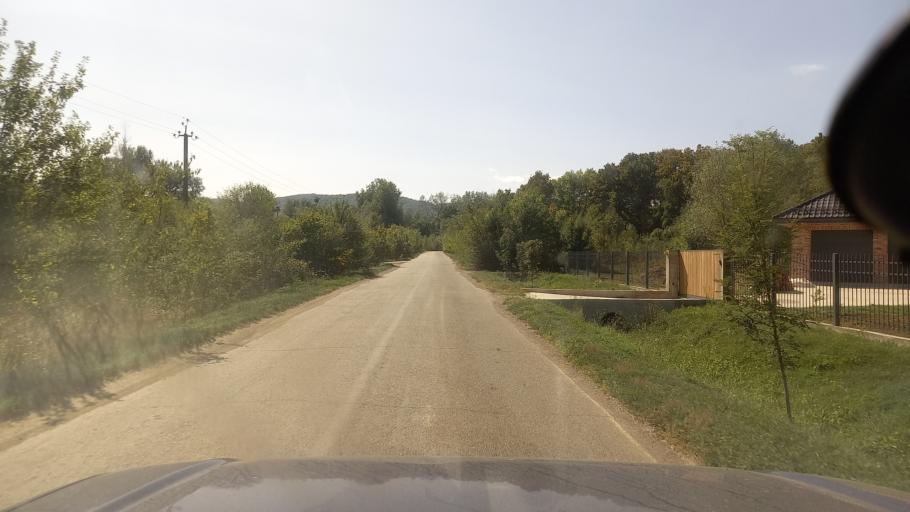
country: RU
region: Krasnodarskiy
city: Azovskaya
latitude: 44.7016
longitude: 38.6701
